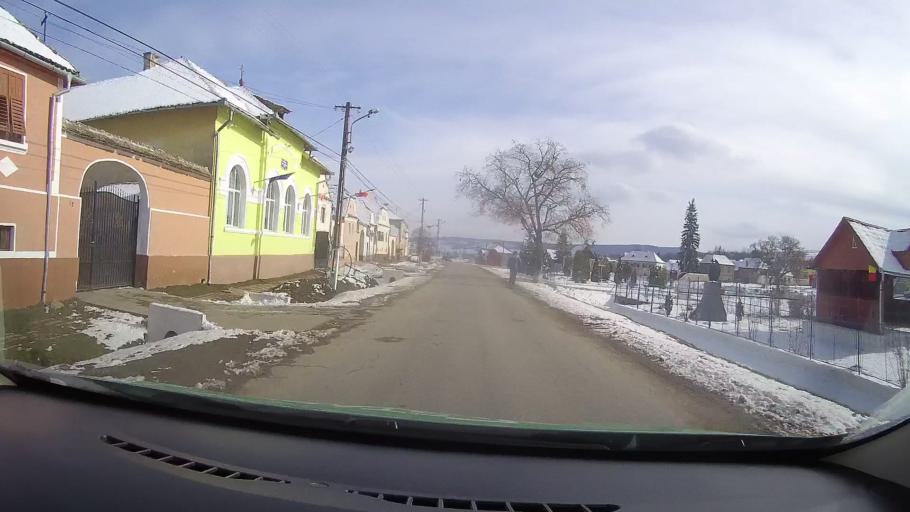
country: RO
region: Sibiu
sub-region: Comuna Iacobeni
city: Iacobeni
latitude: 46.0515
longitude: 24.7161
